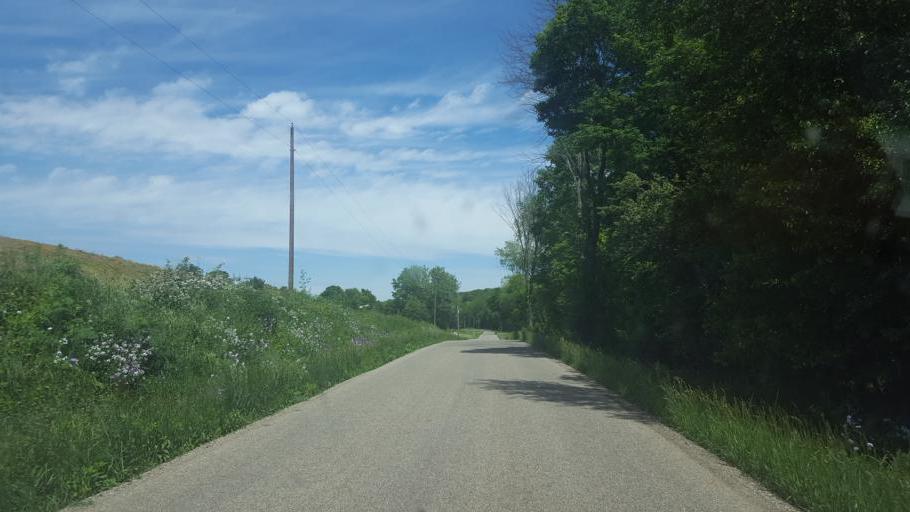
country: US
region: Ohio
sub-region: Knox County
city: Oak Hill
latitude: 40.3828
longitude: -82.3156
